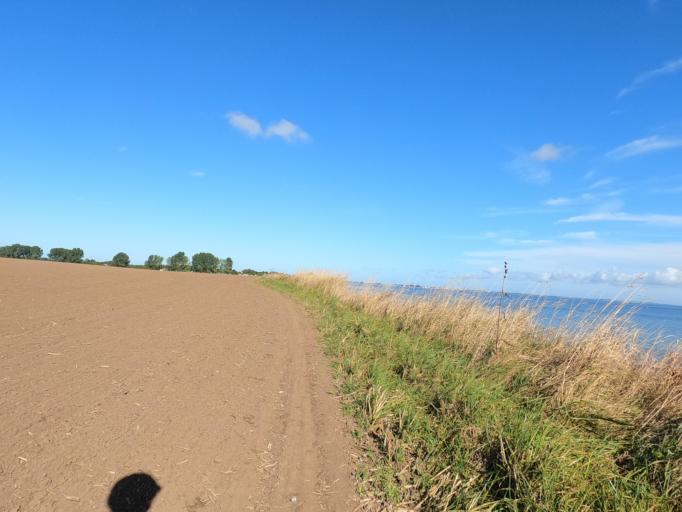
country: DE
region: Schleswig-Holstein
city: Neukirchen
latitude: 54.2968
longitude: 11.0777
